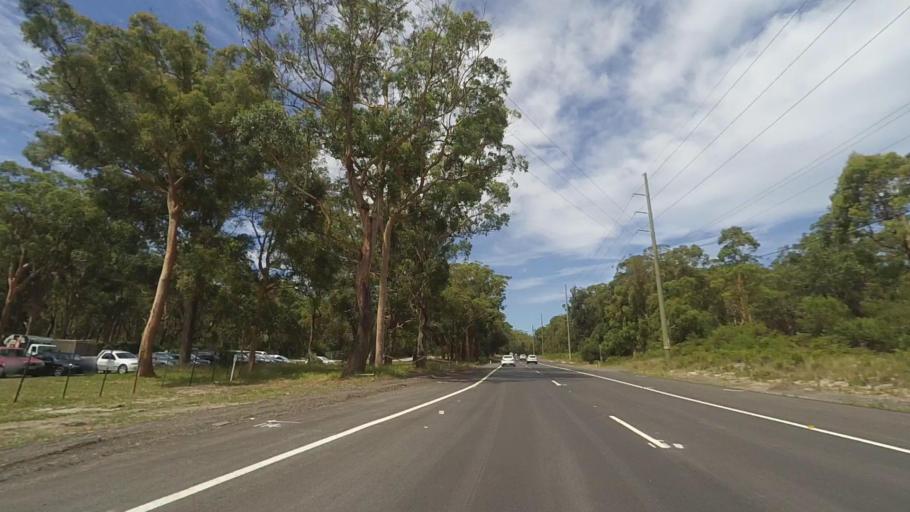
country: AU
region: New South Wales
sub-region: Port Stephens Shire
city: Anna Bay
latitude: -32.7806
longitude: 151.9863
